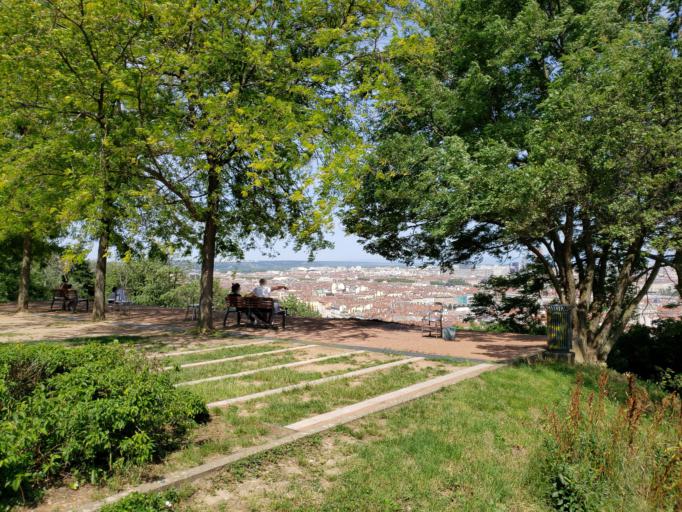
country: FR
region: Rhone-Alpes
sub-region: Departement du Rhone
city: Lyon
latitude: 45.7549
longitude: 4.8219
